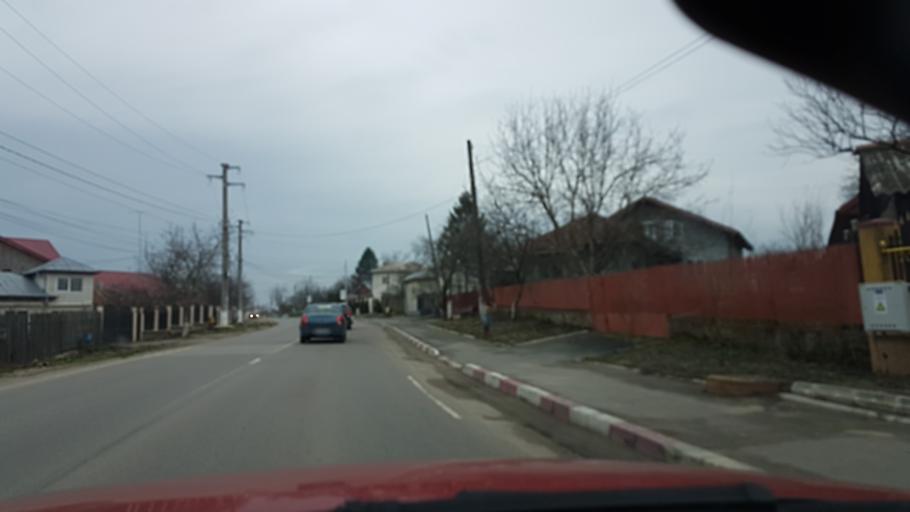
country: RO
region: Ilfov
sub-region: Comuna Balotesti
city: Balotesti
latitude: 44.6218
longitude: 26.1161
